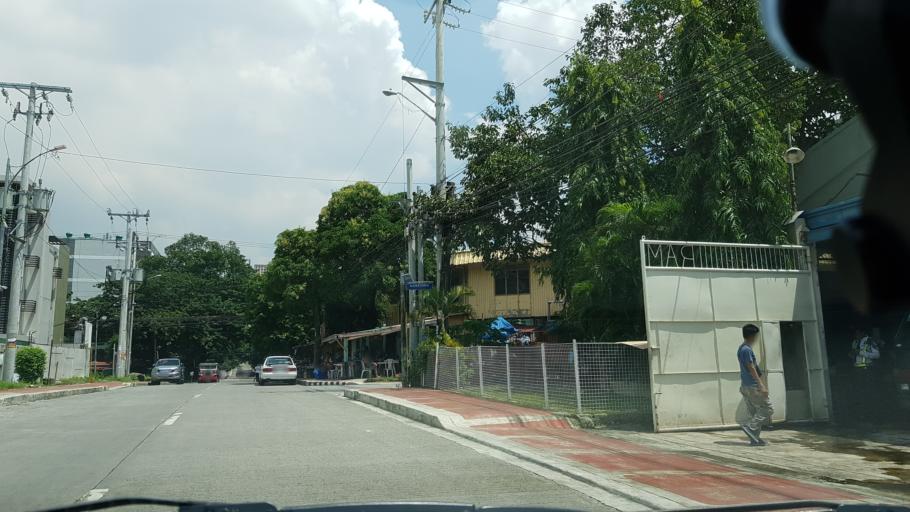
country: PH
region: Calabarzon
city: Del Monte
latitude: 14.6290
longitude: 121.0274
